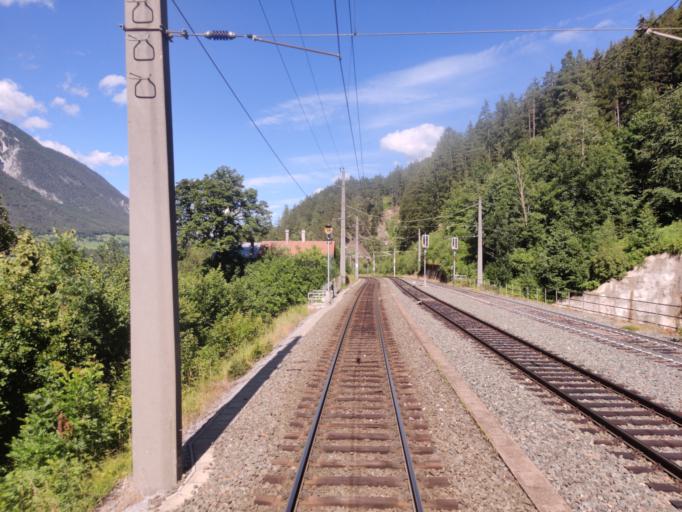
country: AT
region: Tyrol
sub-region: Politischer Bezirk Landeck
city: Pians
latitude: 47.1303
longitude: 10.5107
